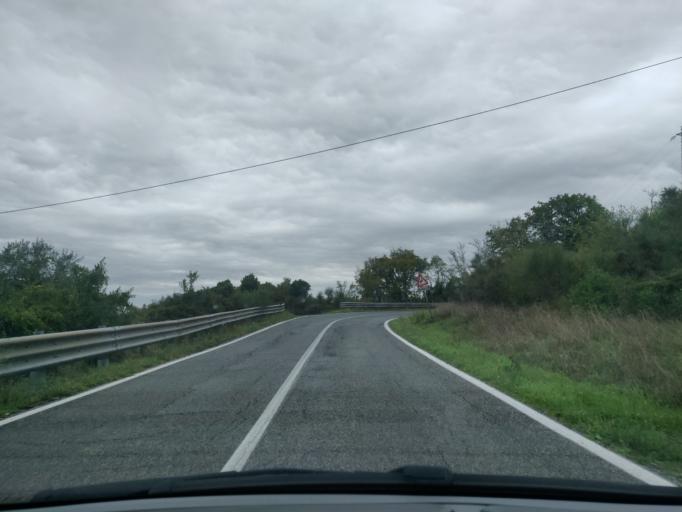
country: IT
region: Latium
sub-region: Citta metropolitana di Roma Capitale
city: Allumiere
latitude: 42.1470
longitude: 11.8960
